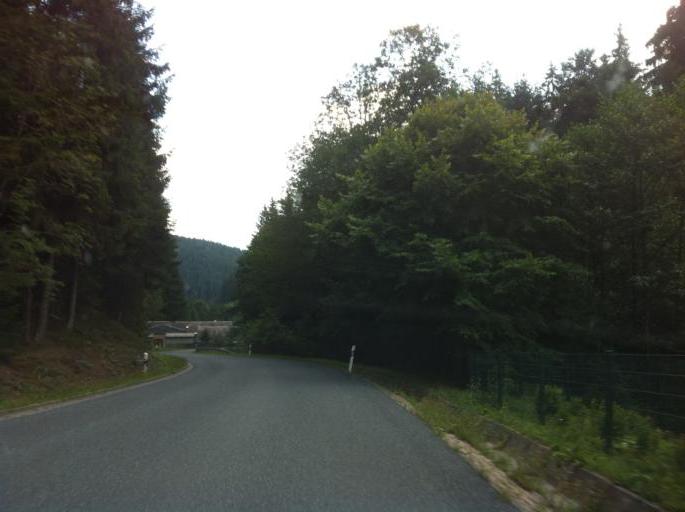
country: DE
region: Thuringia
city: Katzhutte
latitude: 50.5377
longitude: 11.0705
